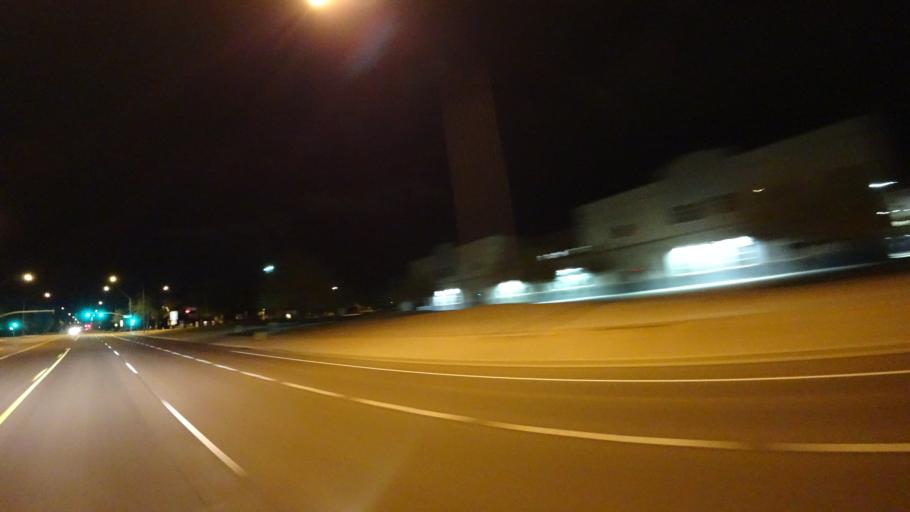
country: US
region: Arizona
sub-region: Pinal County
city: Apache Junction
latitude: 33.3704
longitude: -111.6187
